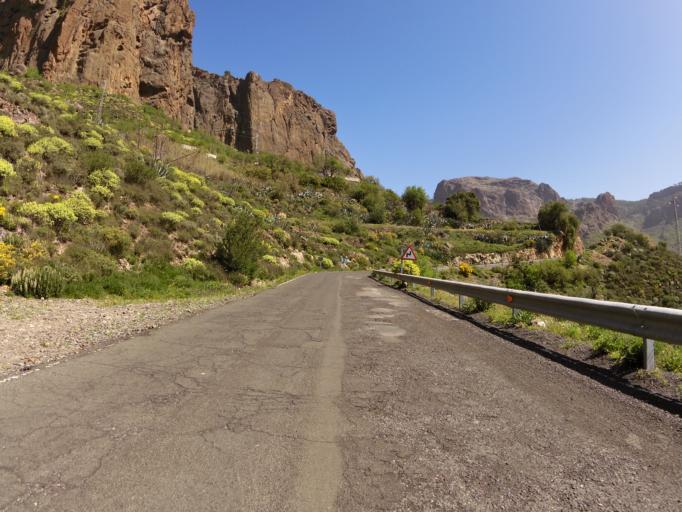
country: ES
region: Canary Islands
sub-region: Provincia de Las Palmas
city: Tejeda
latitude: 27.9539
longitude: -15.6193
